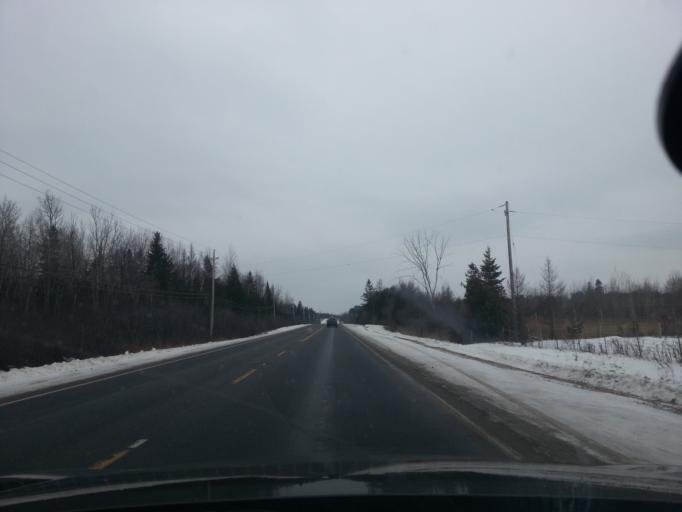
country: CA
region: Ontario
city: Carleton Place
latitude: 45.3058
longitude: -76.0676
